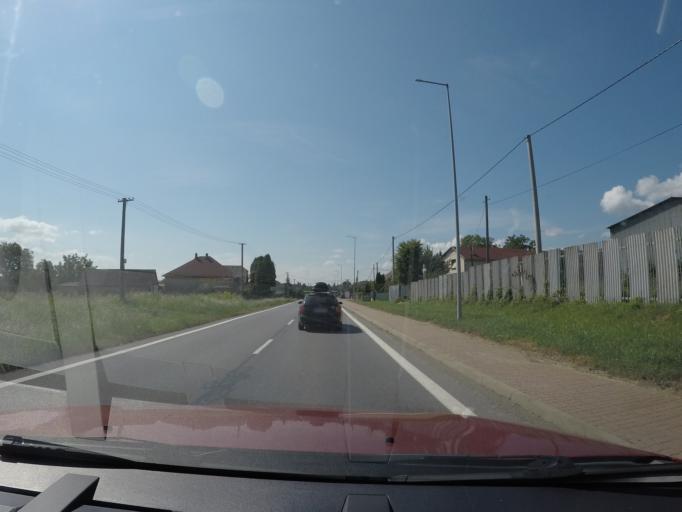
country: SK
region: Presovsky
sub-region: Okres Presov
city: Presov
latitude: 48.9325
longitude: 21.2407
